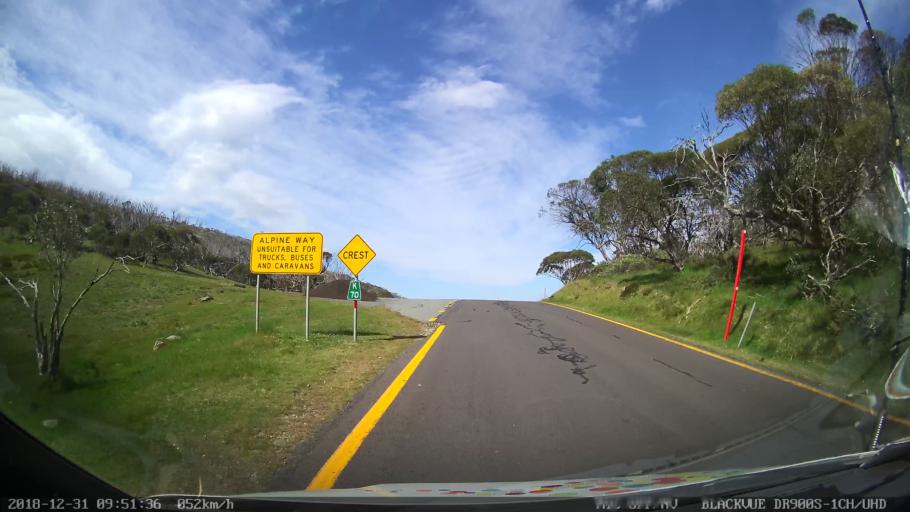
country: AU
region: New South Wales
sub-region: Snowy River
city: Jindabyne
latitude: -36.5238
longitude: 148.2607
